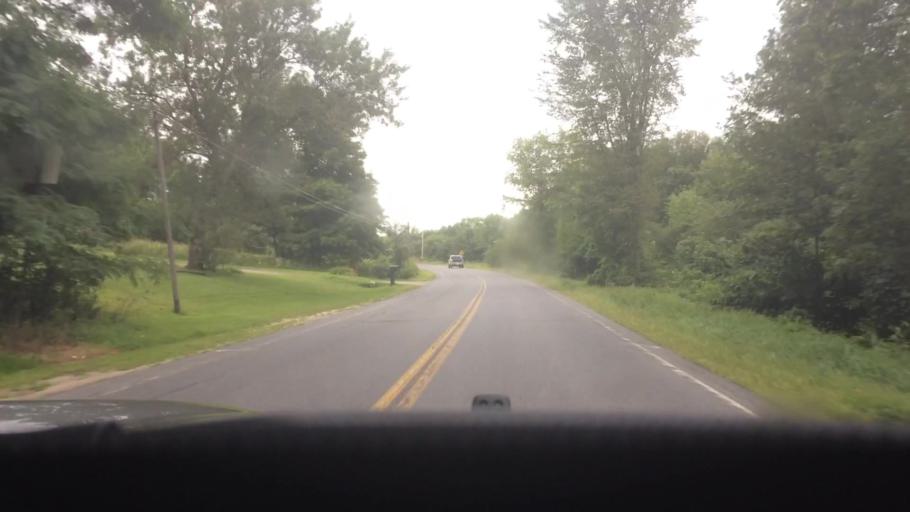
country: US
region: New York
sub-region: St. Lawrence County
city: Canton
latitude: 44.4768
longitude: -75.2262
